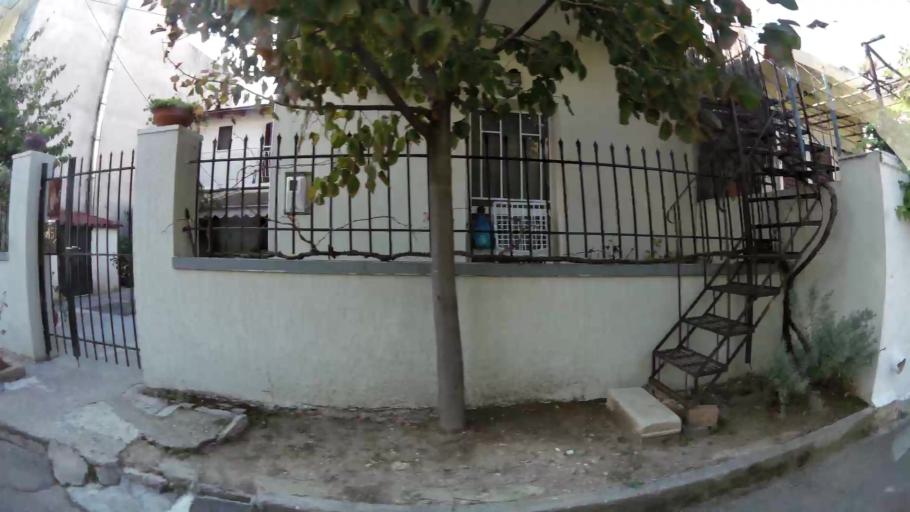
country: GR
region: Attica
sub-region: Nomarchia Athinas
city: Nea Filadelfeia
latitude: 38.0571
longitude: 23.7415
